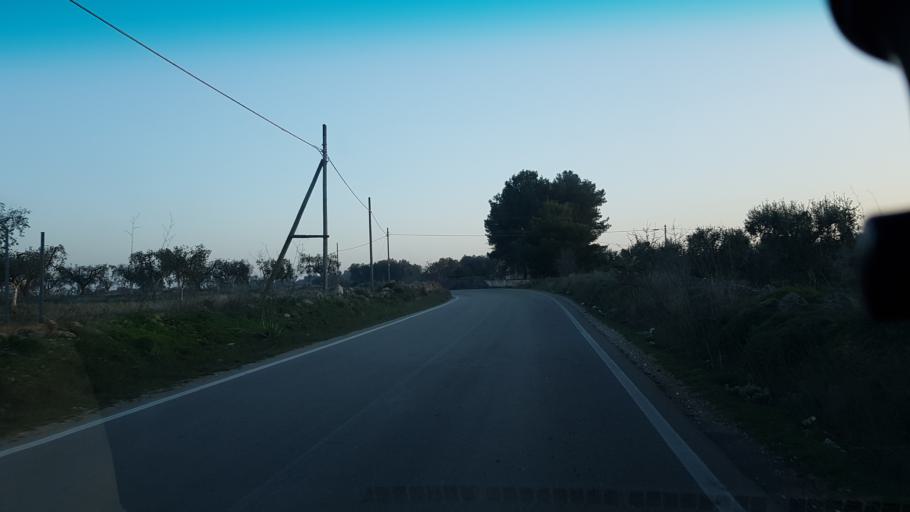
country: IT
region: Apulia
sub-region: Provincia di Brindisi
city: San Vito dei Normanni
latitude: 40.6490
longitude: 17.7757
